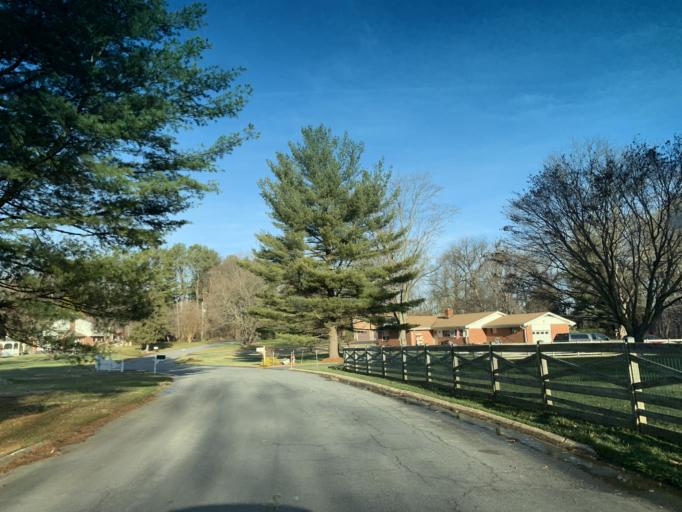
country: US
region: Maryland
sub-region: Harford County
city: Aberdeen
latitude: 39.5743
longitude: -76.1751
